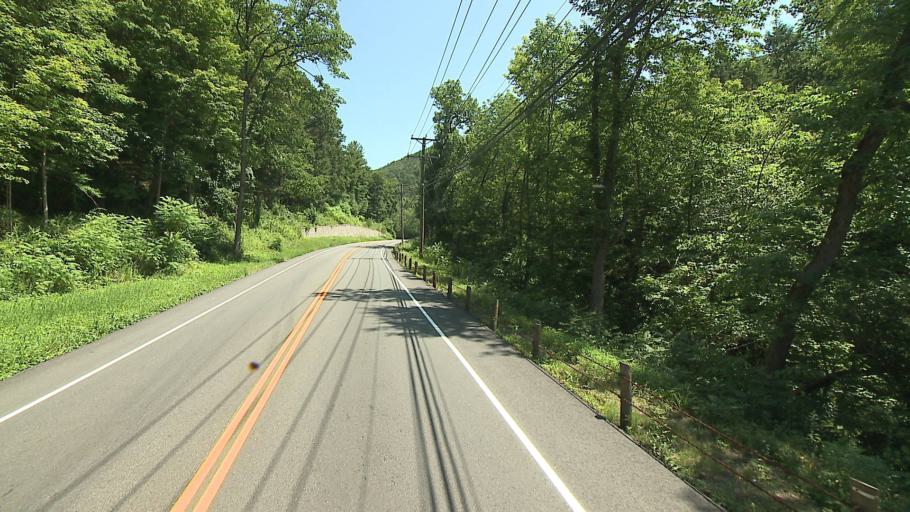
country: US
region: Connecticut
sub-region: Litchfield County
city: New Preston
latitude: 41.8193
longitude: -73.3644
